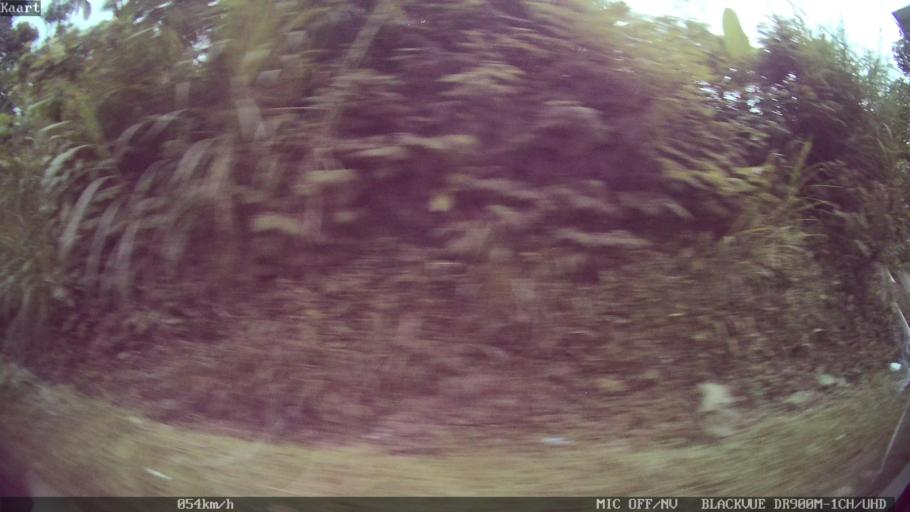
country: ID
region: Bali
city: Banjar Geriana Kangin
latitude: -8.4132
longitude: 115.4378
